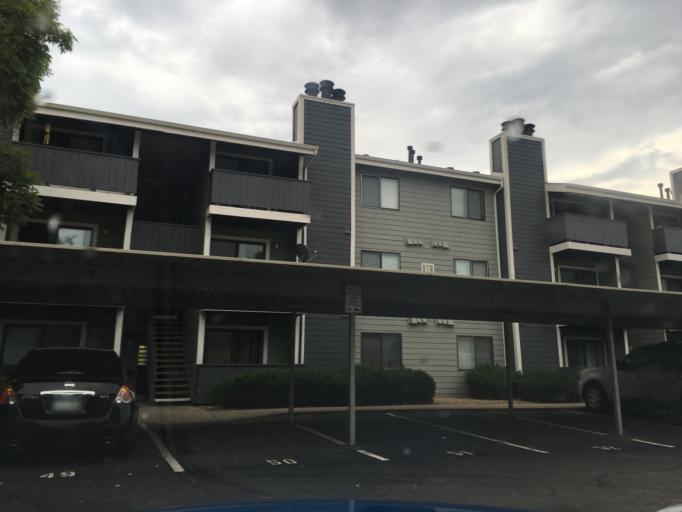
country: US
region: Colorado
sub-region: Arapahoe County
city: Sheridan
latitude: 39.6585
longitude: -105.0293
